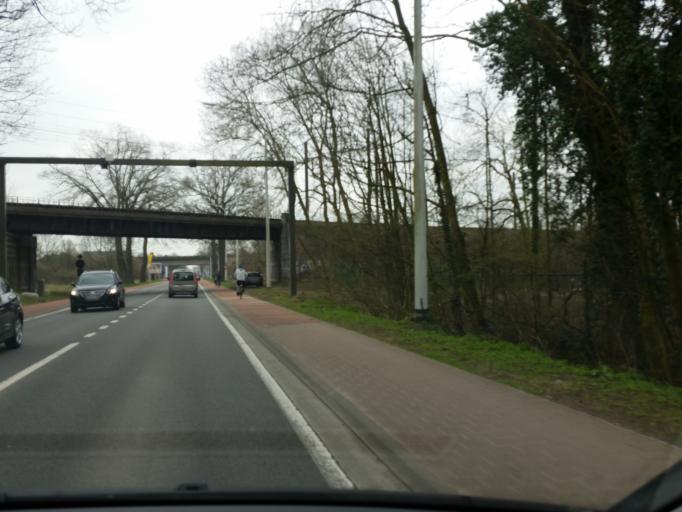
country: BE
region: Flanders
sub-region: Provincie Antwerpen
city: Bonheiden
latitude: 51.0007
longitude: 4.5223
